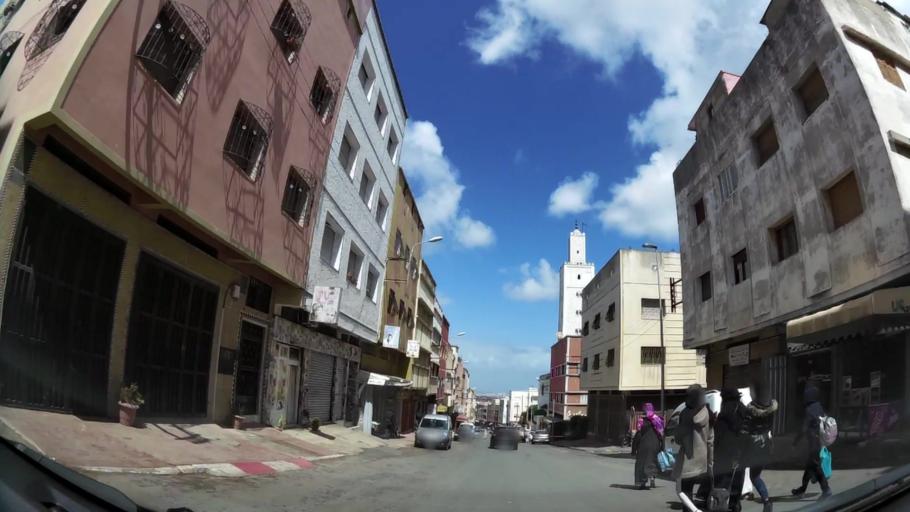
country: MA
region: Grand Casablanca
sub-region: Casablanca
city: Casablanca
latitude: 33.5346
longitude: -7.5842
